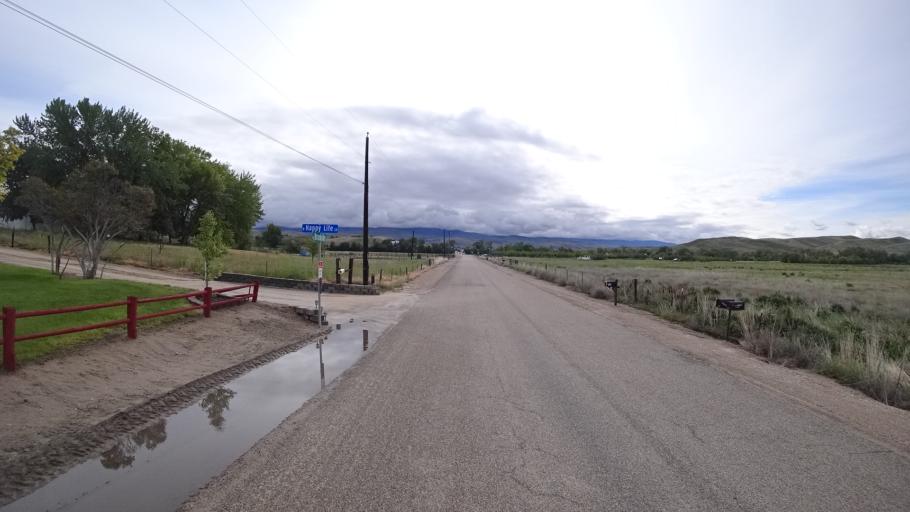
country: US
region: Idaho
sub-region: Ada County
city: Eagle
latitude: 43.7355
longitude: -116.3079
